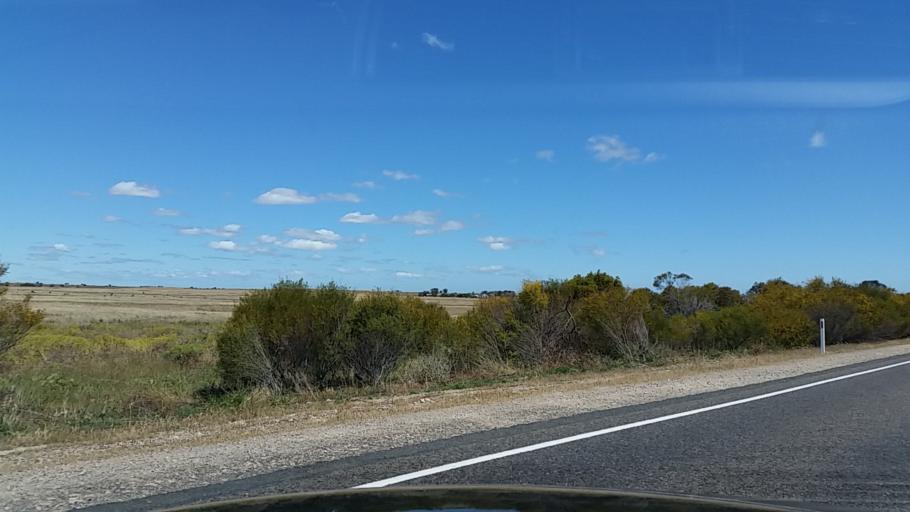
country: AU
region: South Australia
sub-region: Murray Bridge
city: Tailem Bend
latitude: -35.2863
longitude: 139.4505
